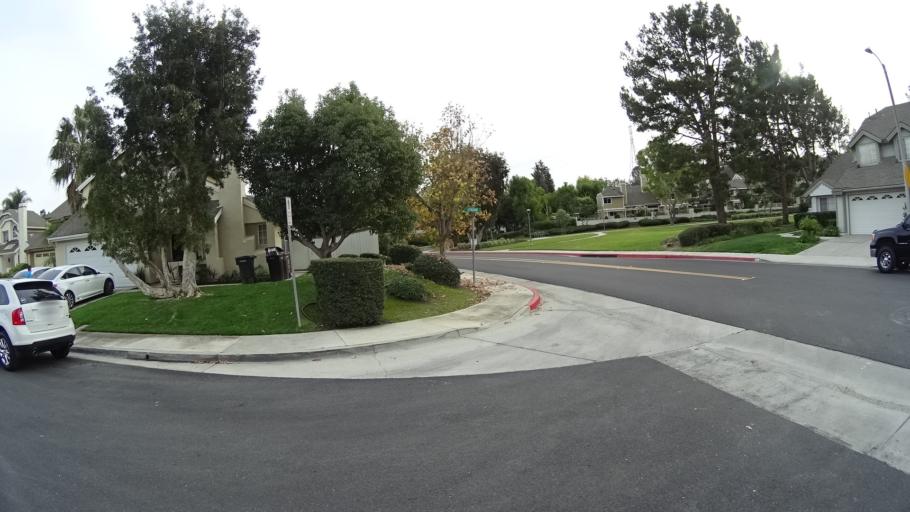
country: US
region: California
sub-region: Orange County
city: Laguna Woods
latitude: 33.5931
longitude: -117.7166
